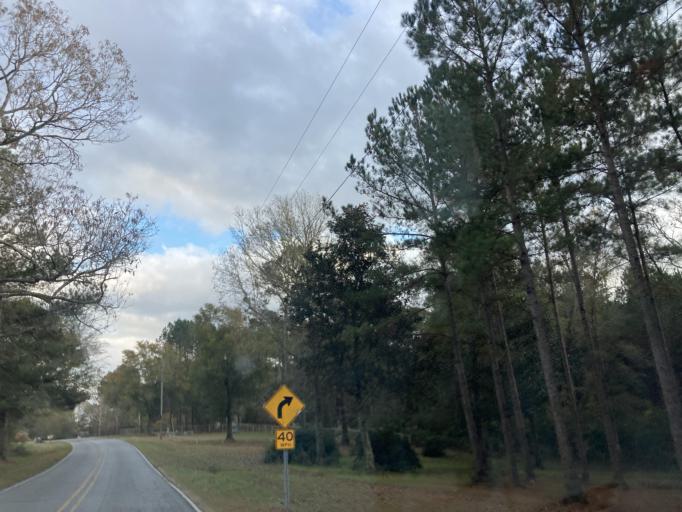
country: US
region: Mississippi
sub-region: Marion County
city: Columbia
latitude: 31.1900
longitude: -89.6692
